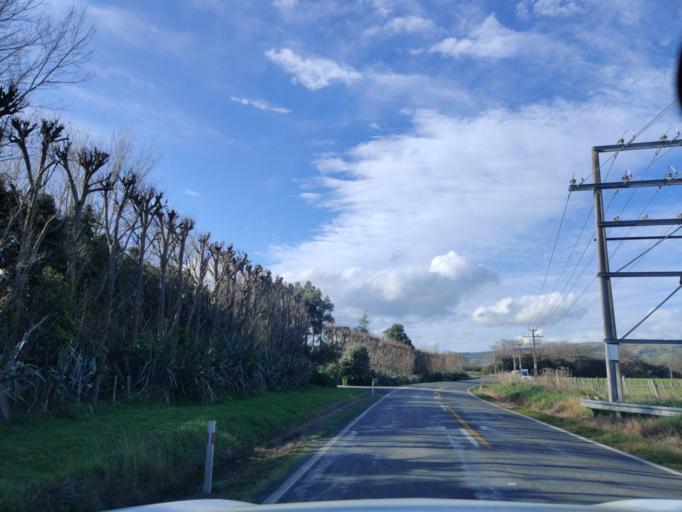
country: NZ
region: Manawatu-Wanganui
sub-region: Palmerston North City
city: Palmerston North
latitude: -40.3363
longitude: 175.7266
